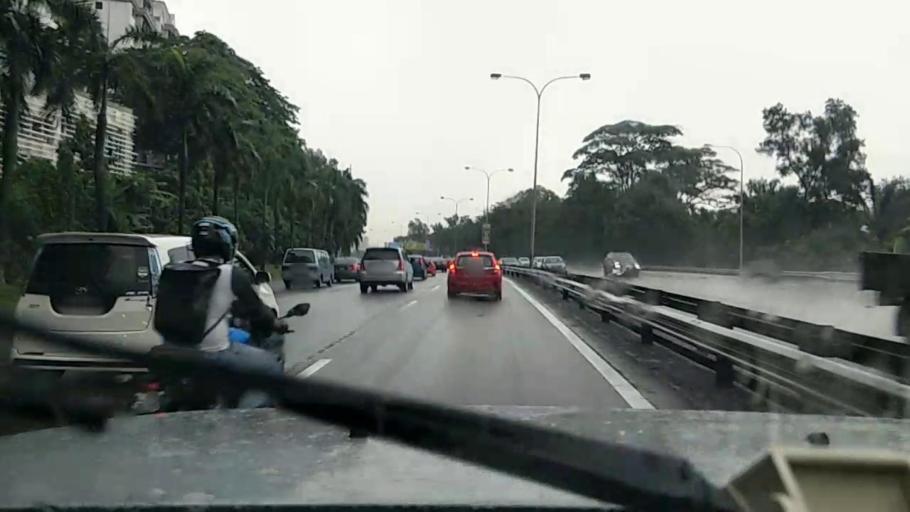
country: MY
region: Kuala Lumpur
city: Kuala Lumpur
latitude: 3.1074
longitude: 101.6924
